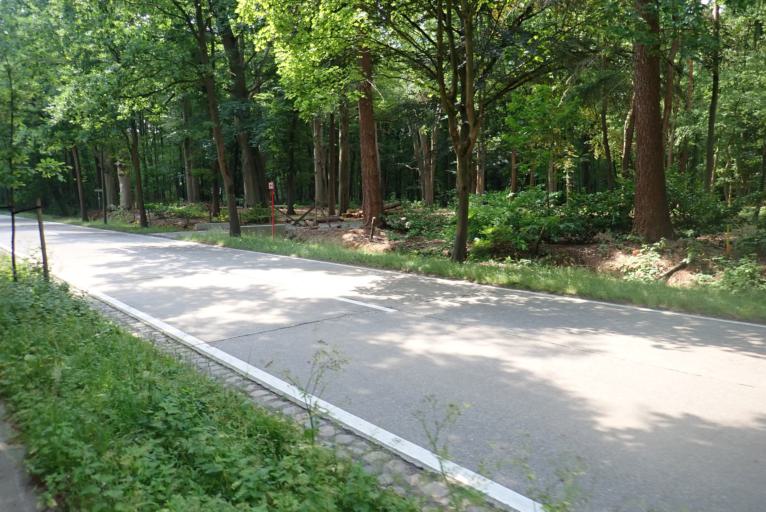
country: BE
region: Flanders
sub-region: Provincie Antwerpen
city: Brecht
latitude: 51.2906
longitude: 4.6286
